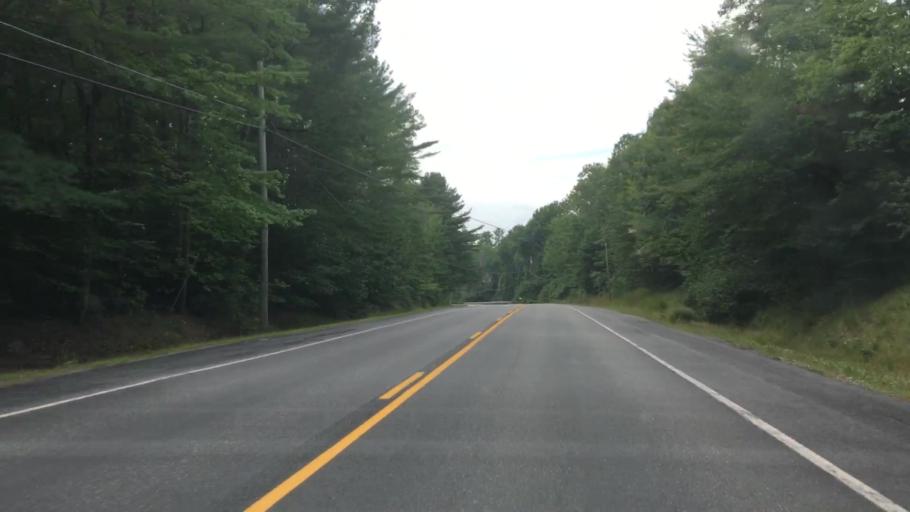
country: US
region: Maine
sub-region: Oxford County
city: Bethel
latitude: 44.4856
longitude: -70.7113
